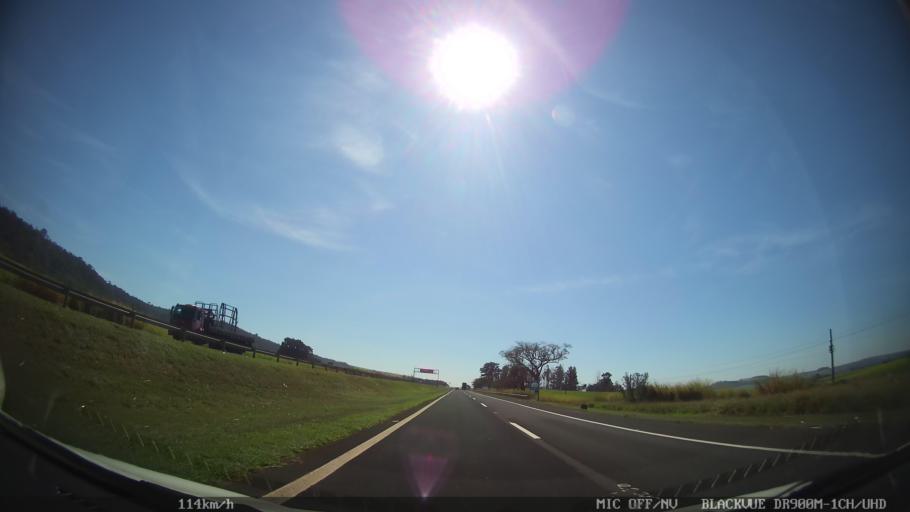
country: BR
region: Sao Paulo
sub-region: Sao Simao
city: Sao Simao
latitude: -21.5214
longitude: -47.6430
